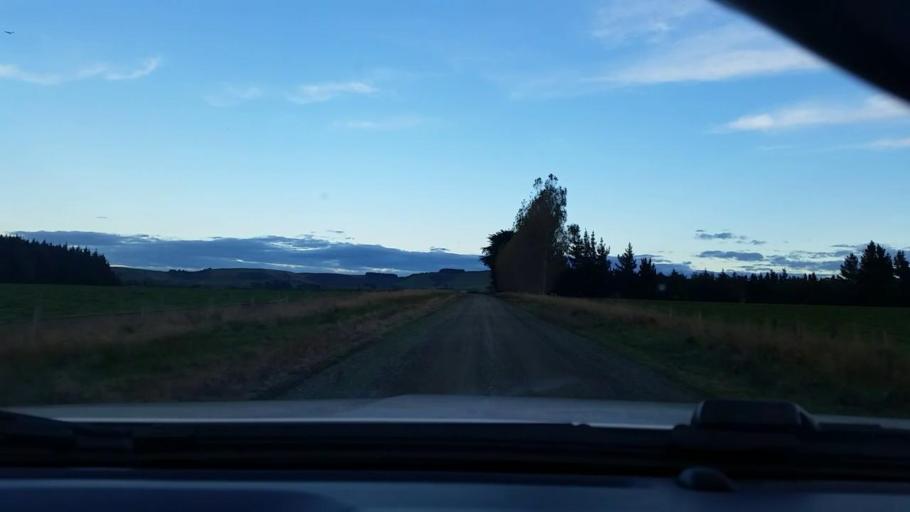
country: NZ
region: Southland
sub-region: Southland District
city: Winton
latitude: -46.1051
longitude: 168.4551
